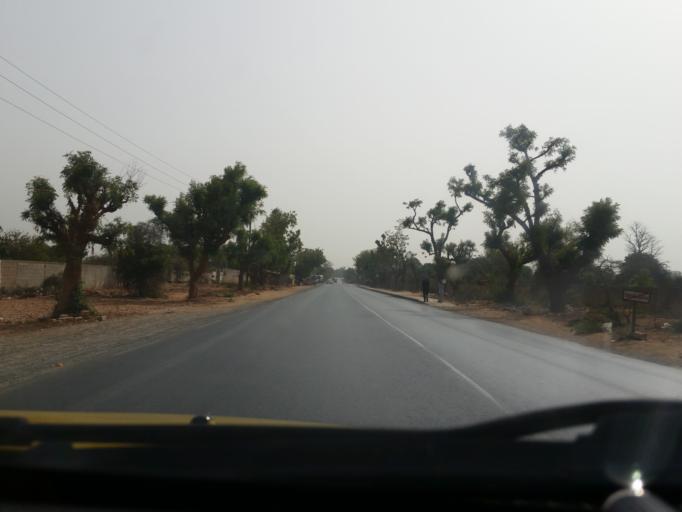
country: SN
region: Thies
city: Pout
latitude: 14.7518
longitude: -17.1281
